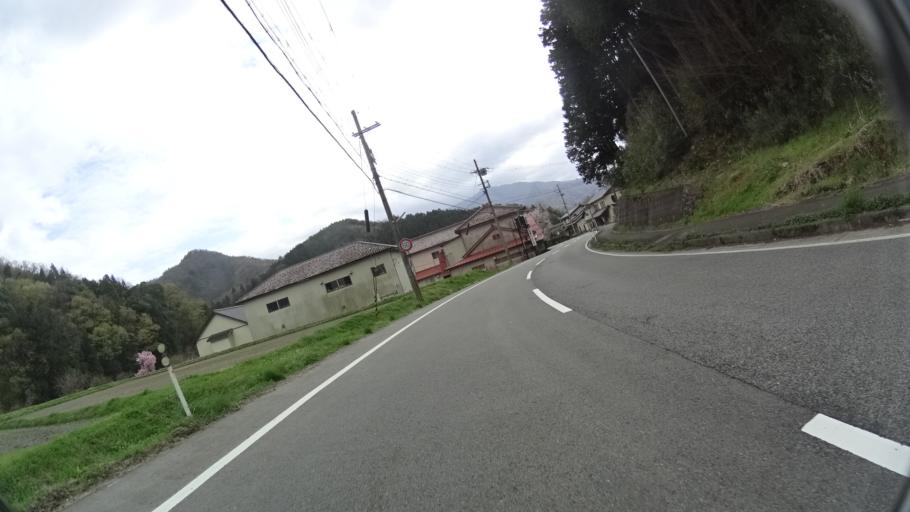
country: JP
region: Hyogo
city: Toyooka
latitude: 35.4664
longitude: 134.9307
